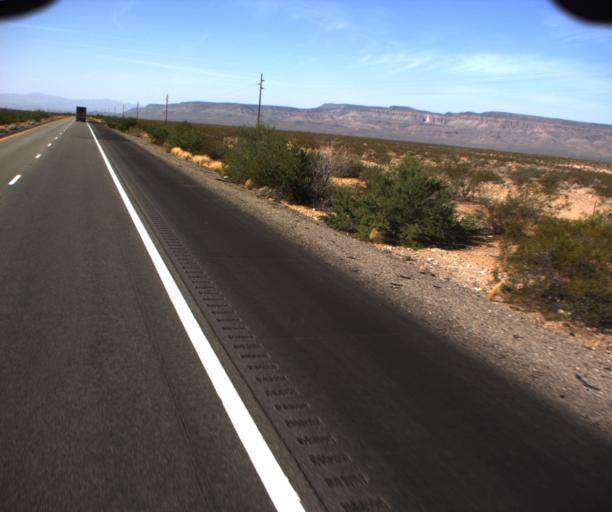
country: US
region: Arizona
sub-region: Mohave County
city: Kingman
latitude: 34.9563
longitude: -114.1452
